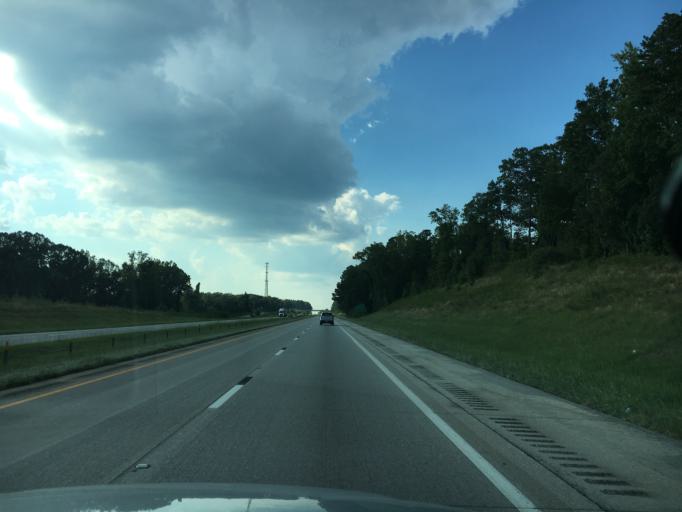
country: US
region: South Carolina
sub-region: Laurens County
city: Watts Mills
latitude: 34.5612
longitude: -82.0220
